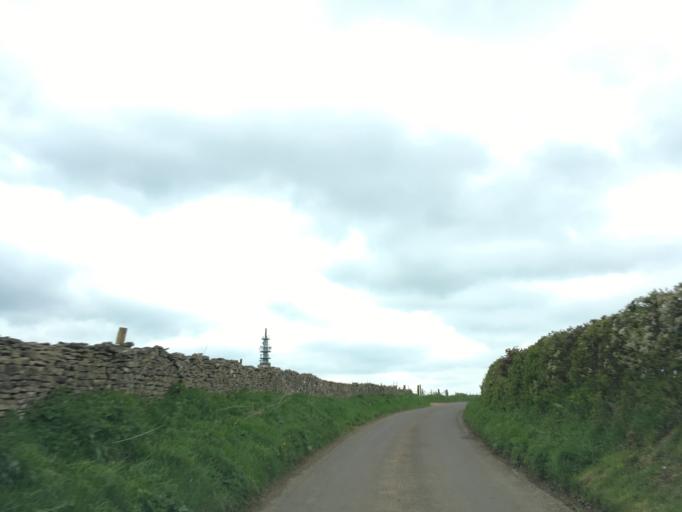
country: GB
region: England
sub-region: Gloucestershire
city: Wotton-under-Edge
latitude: 51.6445
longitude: -2.3055
